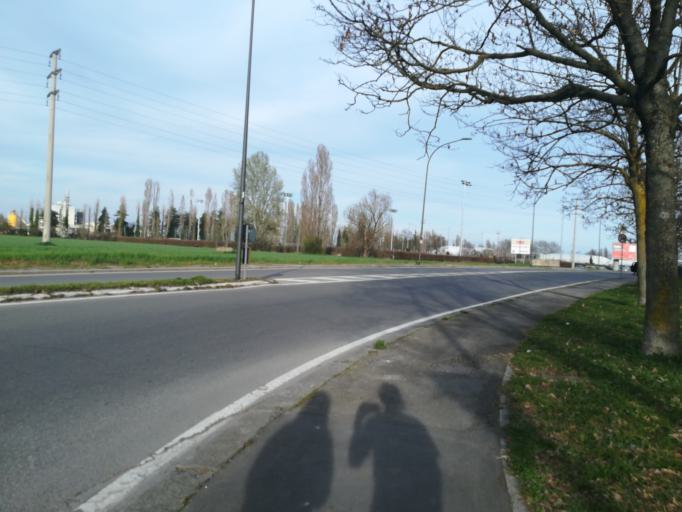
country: IT
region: Emilia-Romagna
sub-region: Provincia di Bologna
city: Progresso
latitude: 44.5505
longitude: 11.3578
